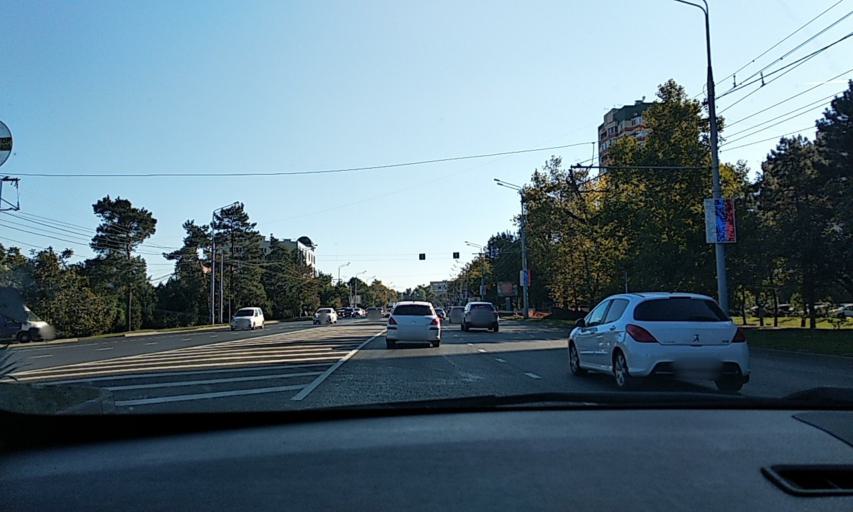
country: RU
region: Krasnodarskiy
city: Pashkovskiy
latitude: 45.0125
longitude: 39.0693
